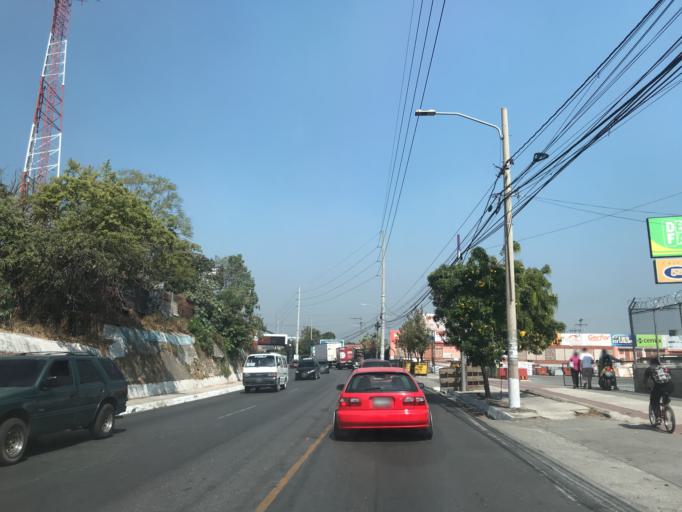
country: GT
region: Guatemala
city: Petapa
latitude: 14.5163
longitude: -90.5638
